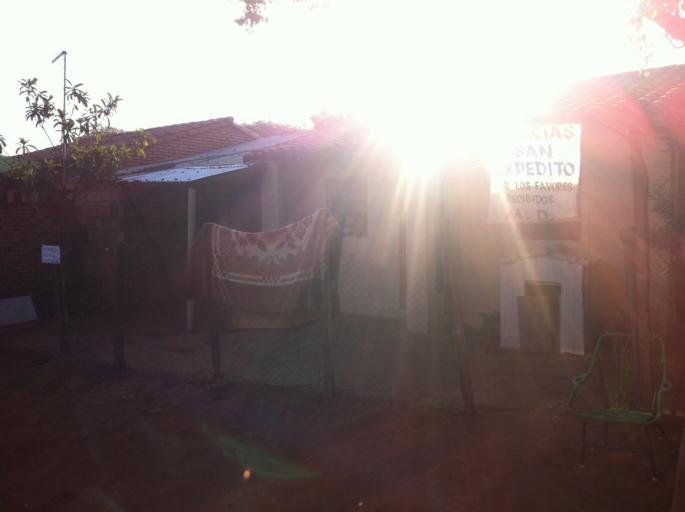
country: PY
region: Central
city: San Lorenzo
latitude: -25.3095
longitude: -57.4913
